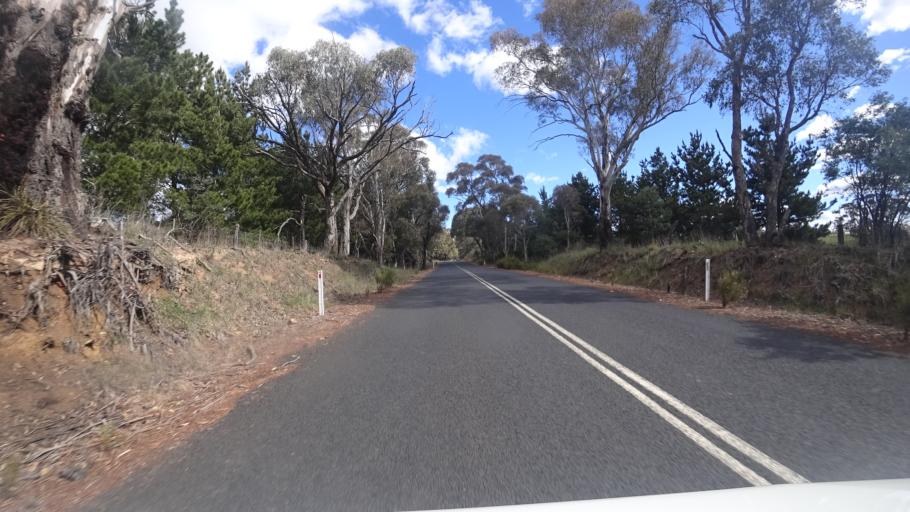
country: AU
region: New South Wales
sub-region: Oberon
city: Oberon
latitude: -33.6819
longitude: 149.7864
